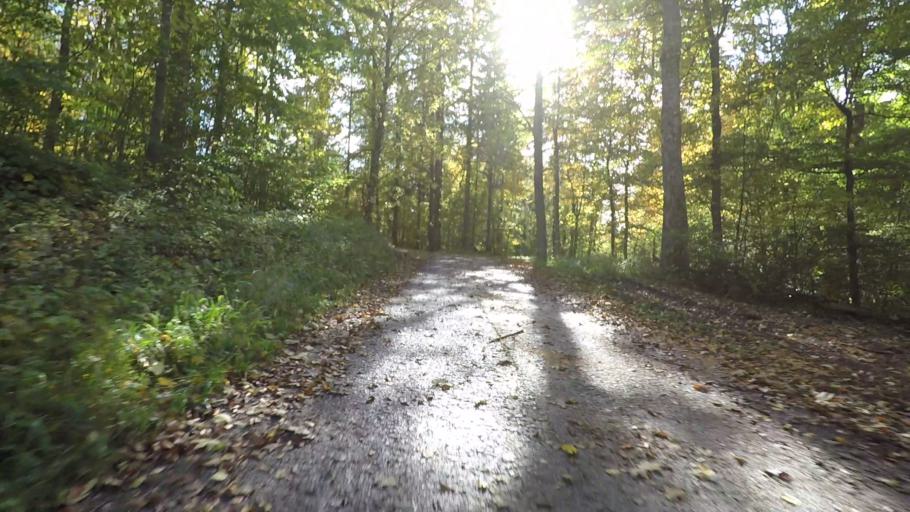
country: DE
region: Baden-Wuerttemberg
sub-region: Tuebingen Region
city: Pfullingen
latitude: 48.4343
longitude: 9.2323
